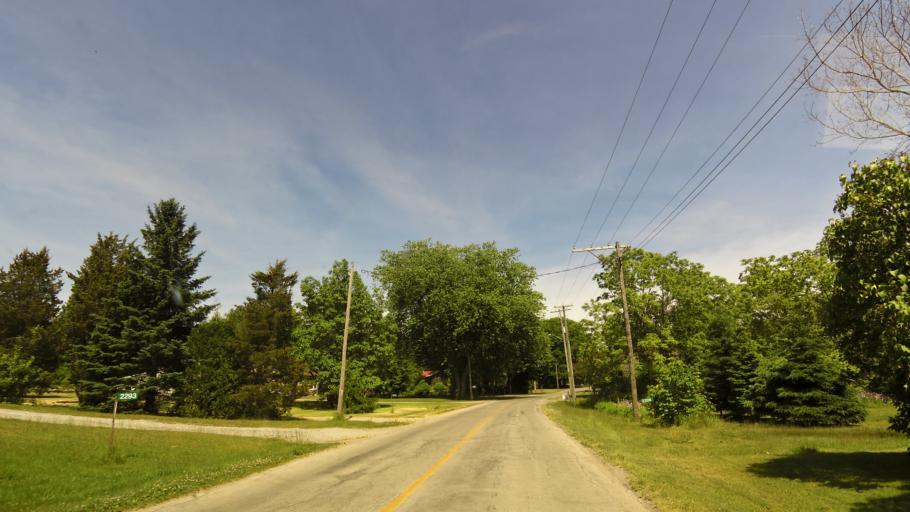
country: CA
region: Ontario
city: Norfolk County
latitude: 42.7109
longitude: -80.3156
